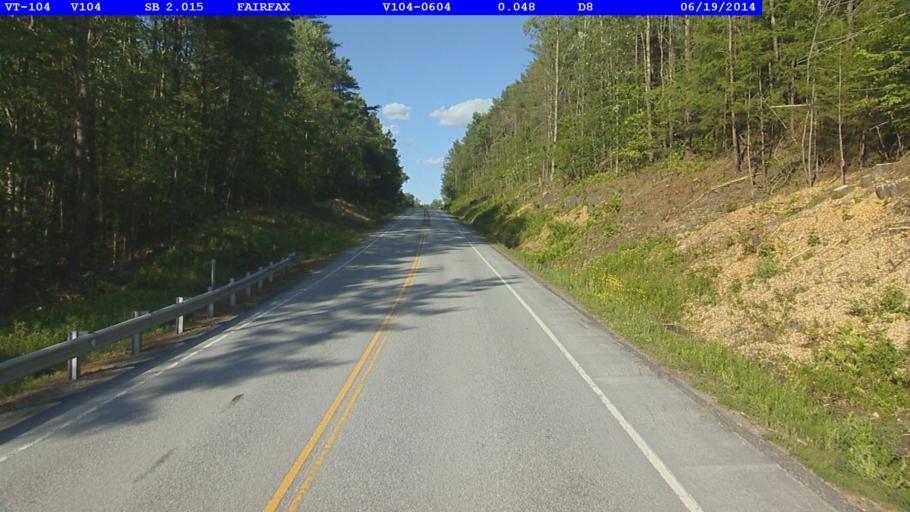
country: US
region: Vermont
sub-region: Chittenden County
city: Jericho
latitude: 44.6388
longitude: -72.9263
